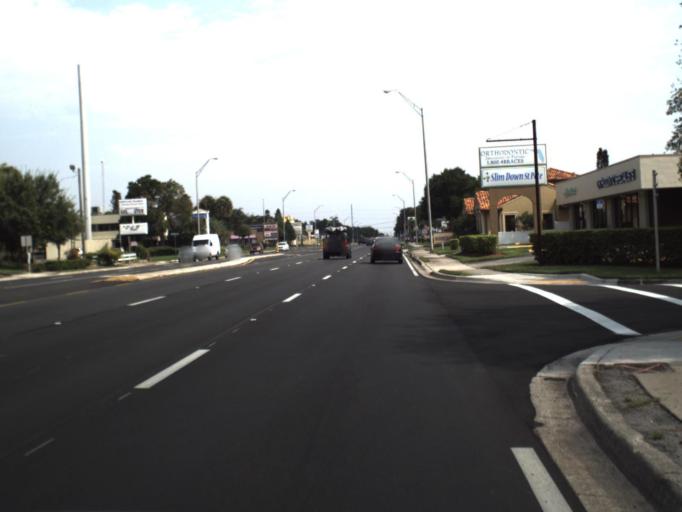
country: US
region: Florida
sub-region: Pinellas County
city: Lealman
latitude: 27.8298
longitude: -82.6386
